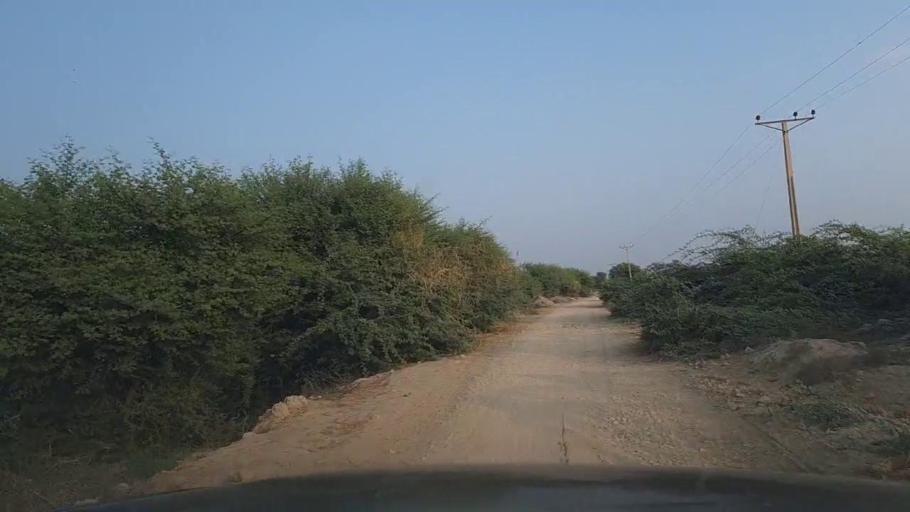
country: PK
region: Sindh
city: Mirpur Batoro
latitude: 24.5446
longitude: 68.3576
